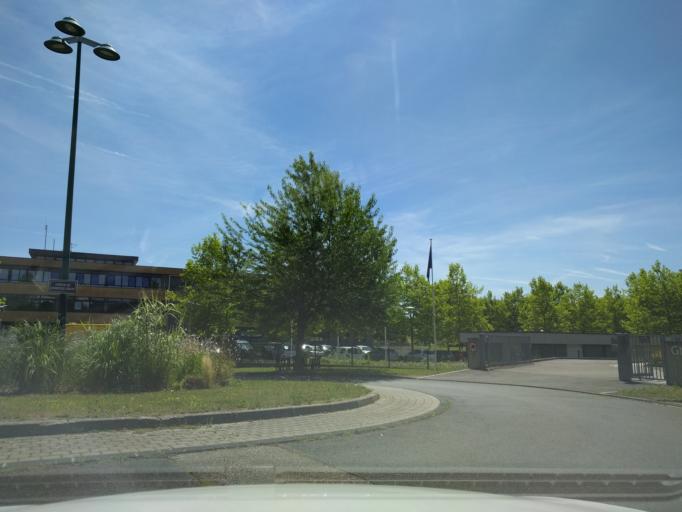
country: FR
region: Lorraine
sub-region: Departement de la Moselle
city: Saint-Julien-les-Metz
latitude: 49.1036
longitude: 6.2094
